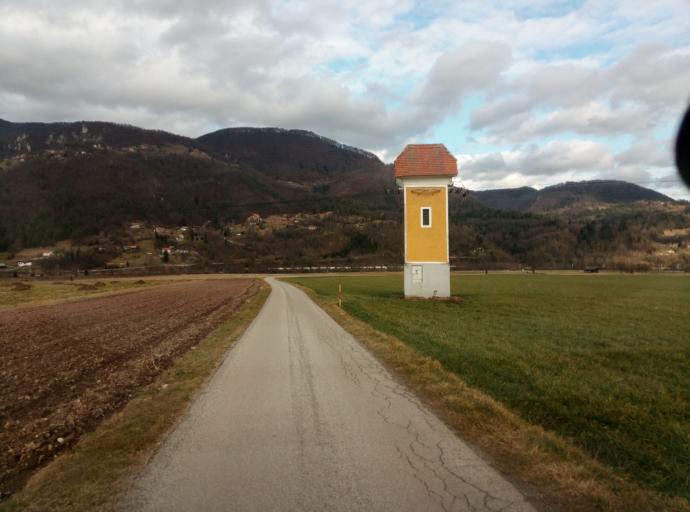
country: SI
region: Radece
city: Radece
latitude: 46.0555
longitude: 15.1930
